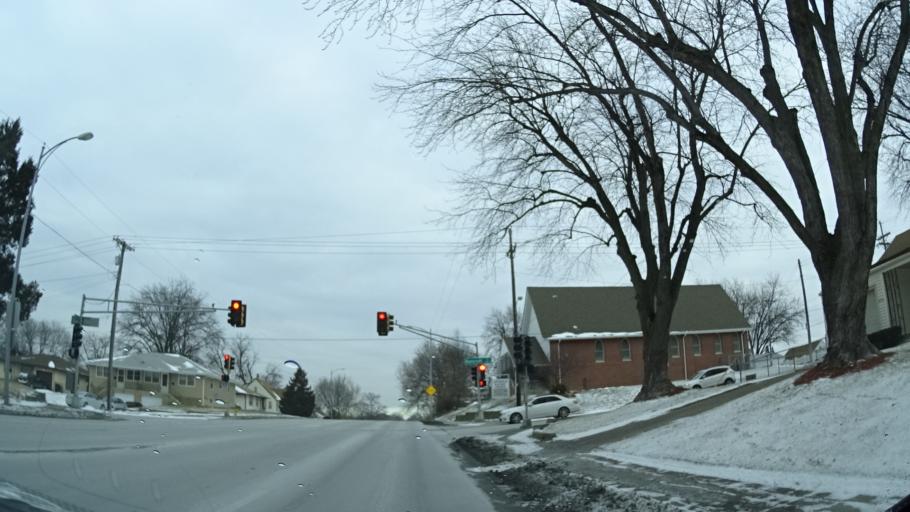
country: US
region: Nebraska
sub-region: Douglas County
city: Omaha
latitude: 41.2339
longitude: -95.9758
